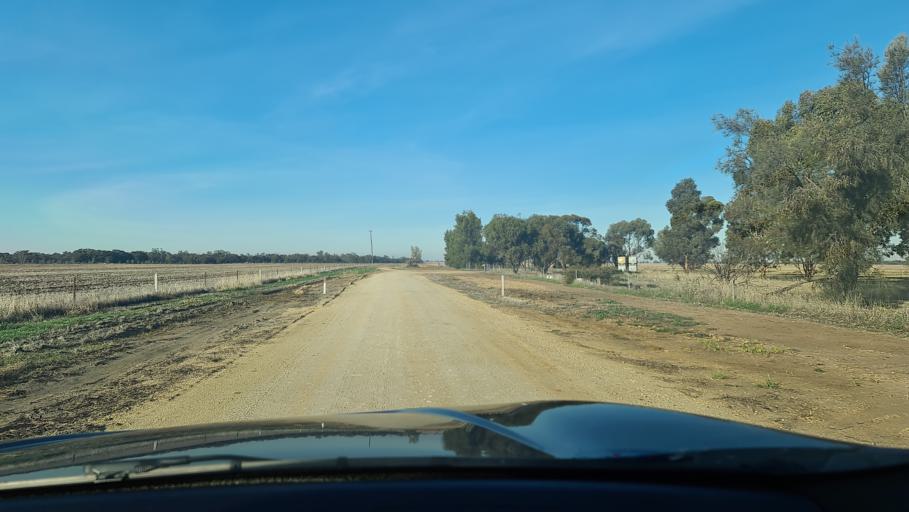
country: AU
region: Victoria
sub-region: Horsham
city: Horsham
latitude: -36.3642
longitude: 142.3956
